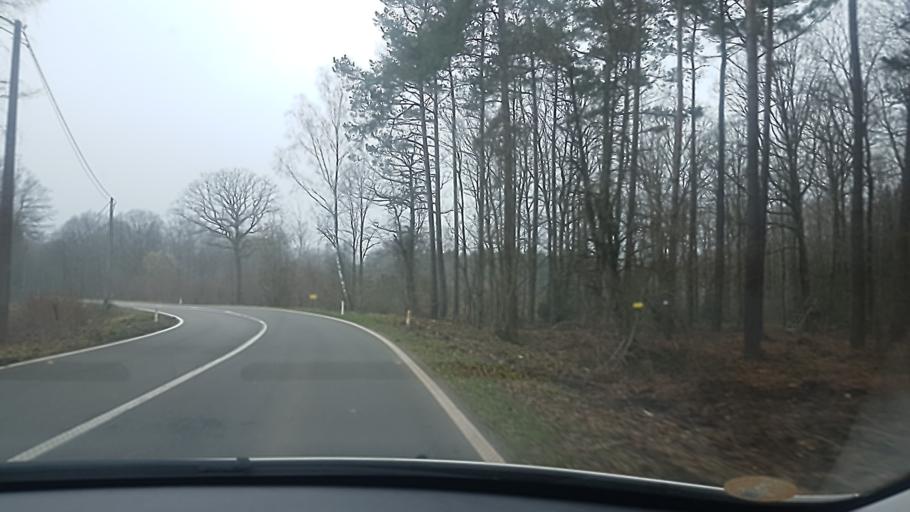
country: FR
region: Champagne-Ardenne
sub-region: Departement des Ardennes
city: Haybes
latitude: 50.0281
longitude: 4.6275
